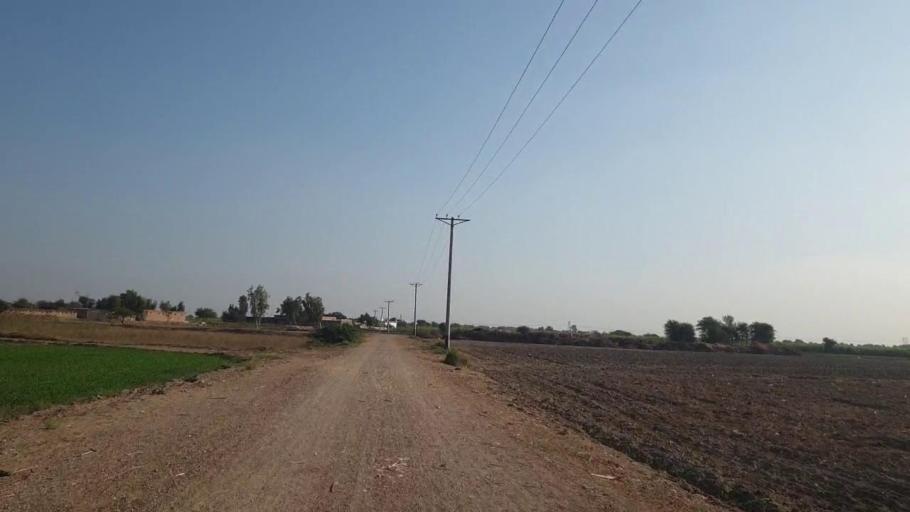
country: PK
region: Sindh
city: Matiari
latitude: 25.4970
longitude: 68.4365
